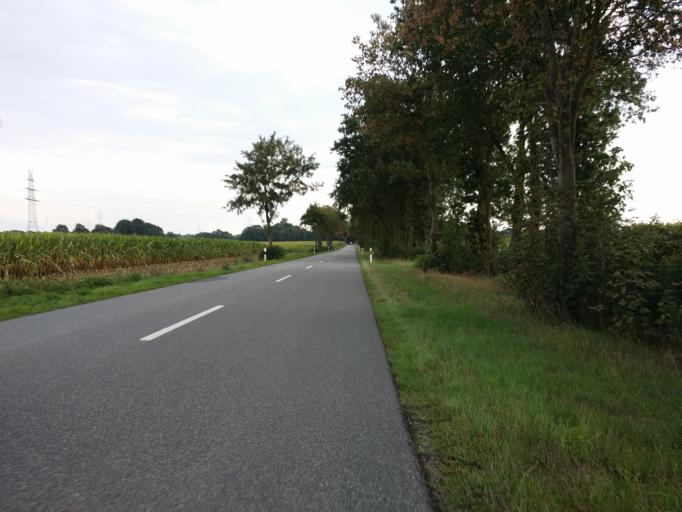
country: DE
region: Lower Saxony
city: Hollnseth
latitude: 53.5804
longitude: 9.1109
